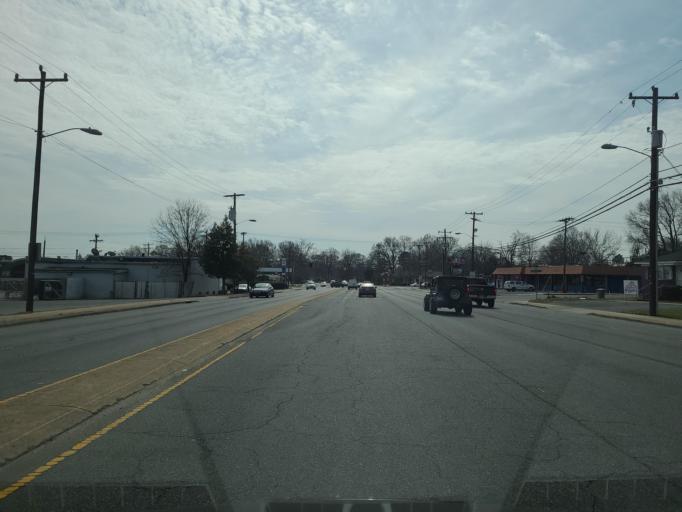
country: US
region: North Carolina
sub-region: Mecklenburg County
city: Charlotte
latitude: 35.2508
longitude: -80.7807
